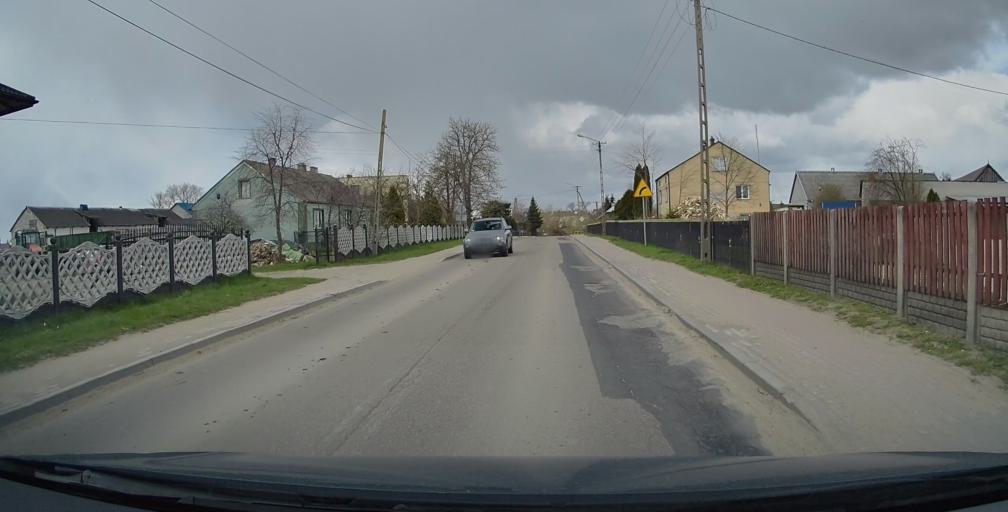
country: PL
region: Masovian Voivodeship
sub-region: Powiat ostrolecki
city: Goworowo
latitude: 52.8986
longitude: 21.5663
